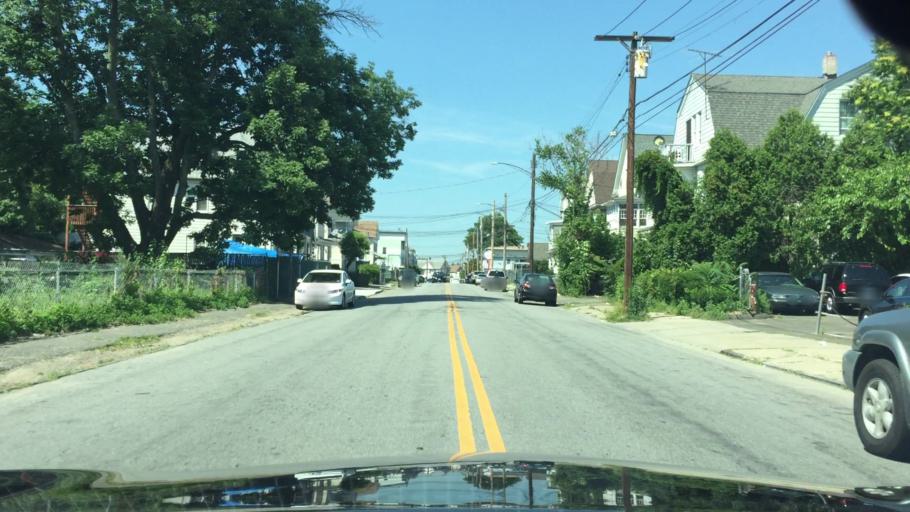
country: US
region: Connecticut
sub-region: Fairfield County
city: Bridgeport
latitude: 41.1834
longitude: -73.2021
